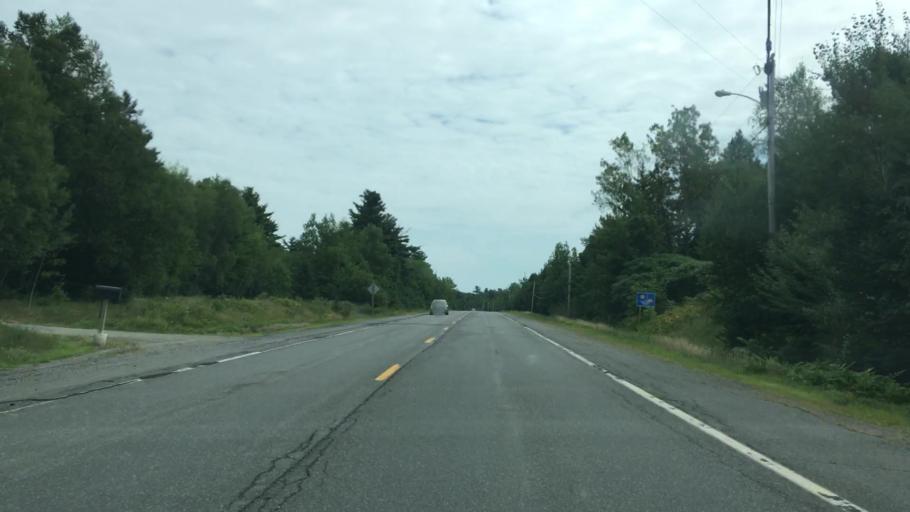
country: US
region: Maine
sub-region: Washington County
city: Calais
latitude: 45.1126
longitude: -67.4191
